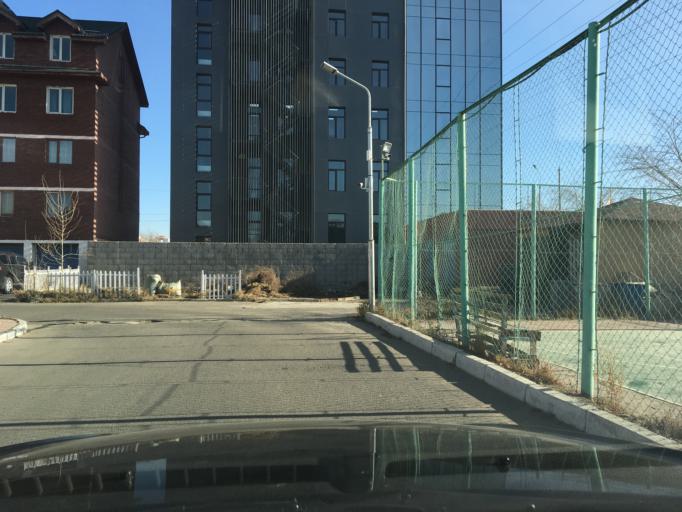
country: MN
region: Ulaanbaatar
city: Ulaanbaatar
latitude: 47.8911
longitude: 106.9084
